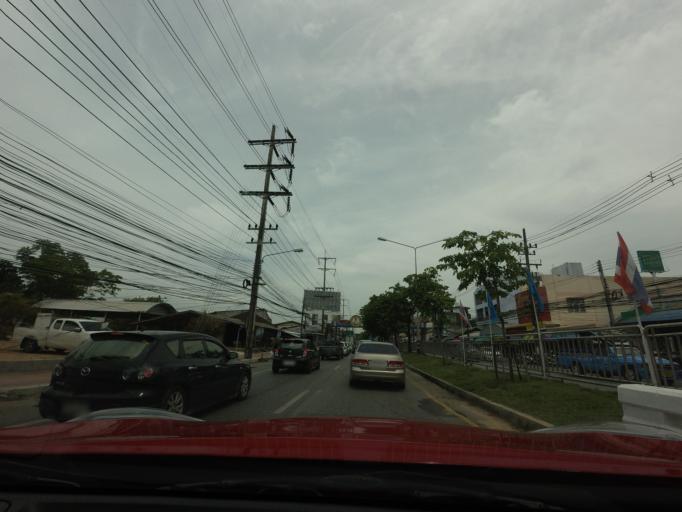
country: TH
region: Songkhla
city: Hat Yai
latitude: 7.0004
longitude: 100.4901
